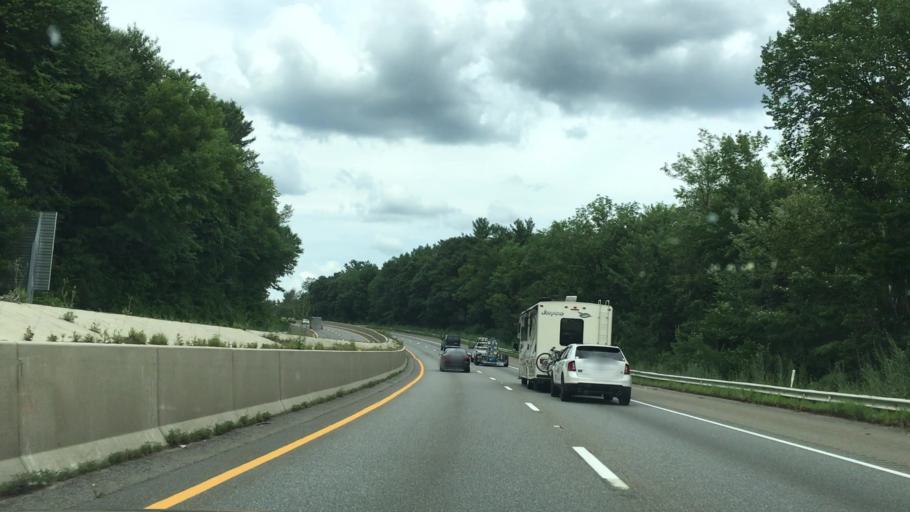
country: US
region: Massachusetts
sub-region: Worcester County
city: Leominster
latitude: 42.5509
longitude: -71.7665
